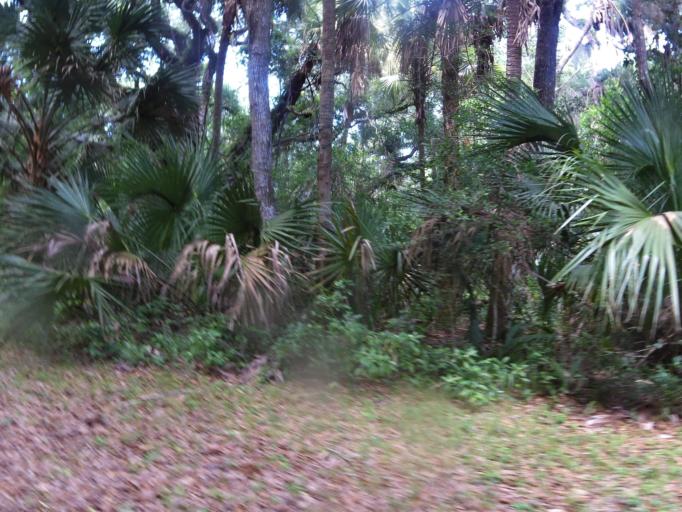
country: US
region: Florida
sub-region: Flagler County
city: Palm Coast
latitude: 29.6354
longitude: -81.2089
